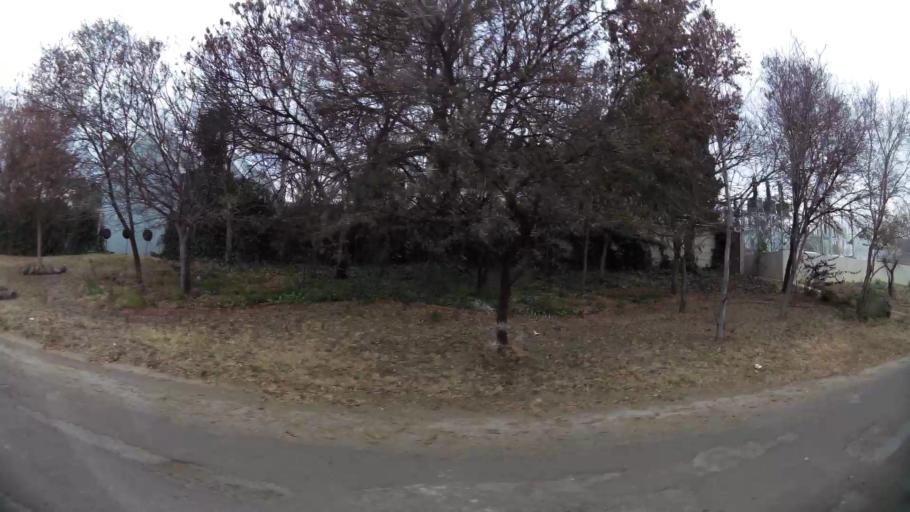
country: ZA
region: Orange Free State
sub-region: Fezile Dabi District Municipality
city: Kroonstad
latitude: -27.6855
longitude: 27.2387
